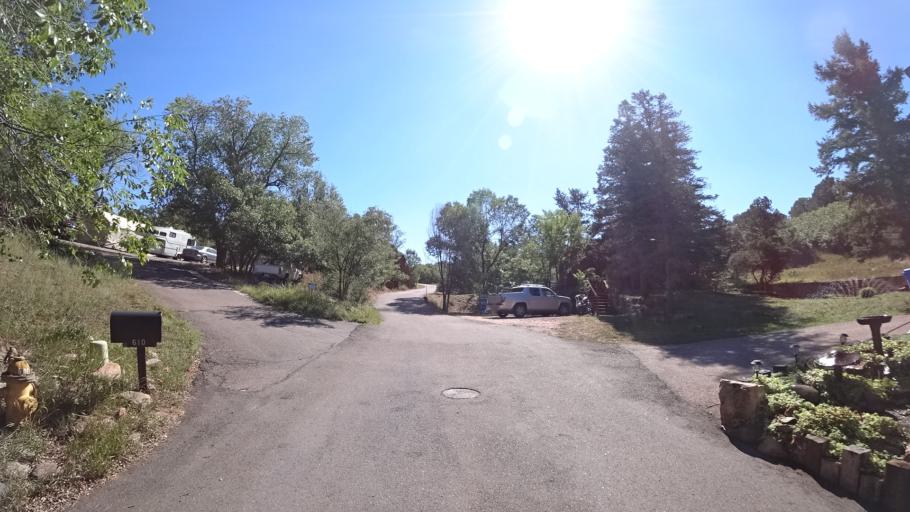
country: US
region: Colorado
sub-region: El Paso County
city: Manitou Springs
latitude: 38.8638
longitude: -104.8826
